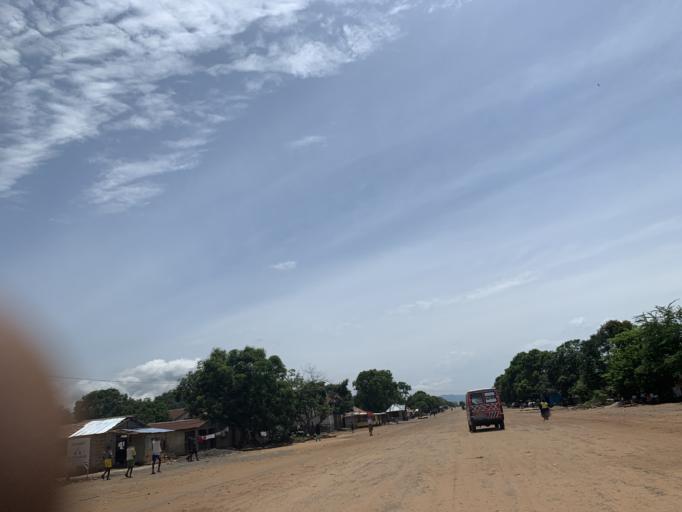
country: SL
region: Western Area
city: Waterloo
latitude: 8.3376
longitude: -13.0440
